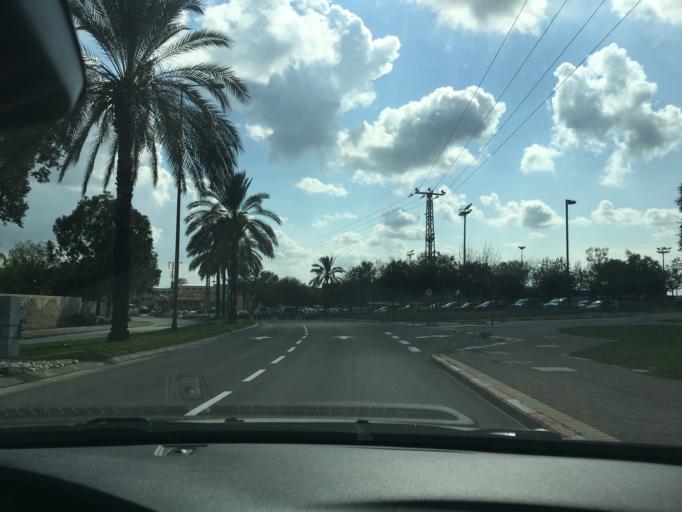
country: IL
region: Central District
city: Kfar Saba
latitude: 32.1807
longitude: 34.9279
